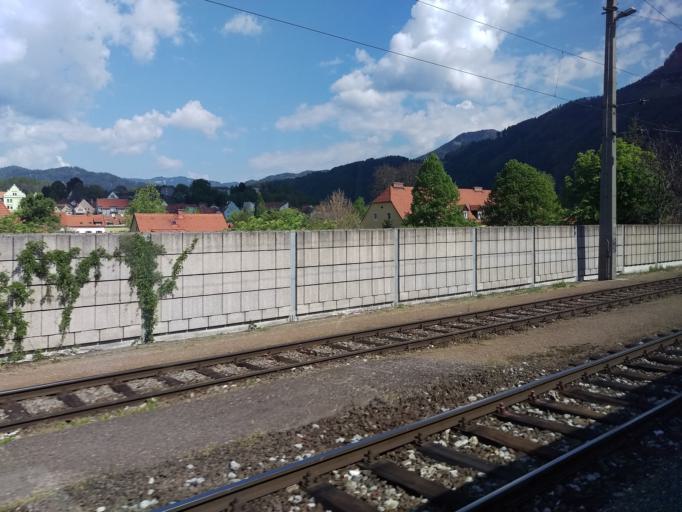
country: AT
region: Styria
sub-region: Politischer Bezirk Graz-Umgebung
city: Frohnleiten
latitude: 47.2670
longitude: 15.3280
